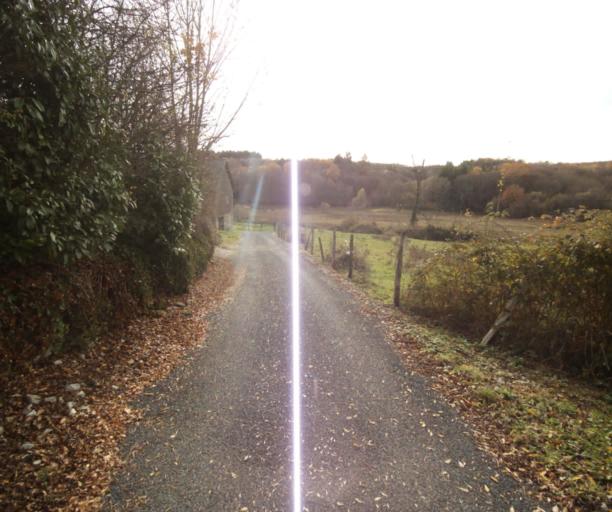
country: FR
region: Limousin
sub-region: Departement de la Correze
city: Beynat
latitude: 45.1718
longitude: 1.7325
